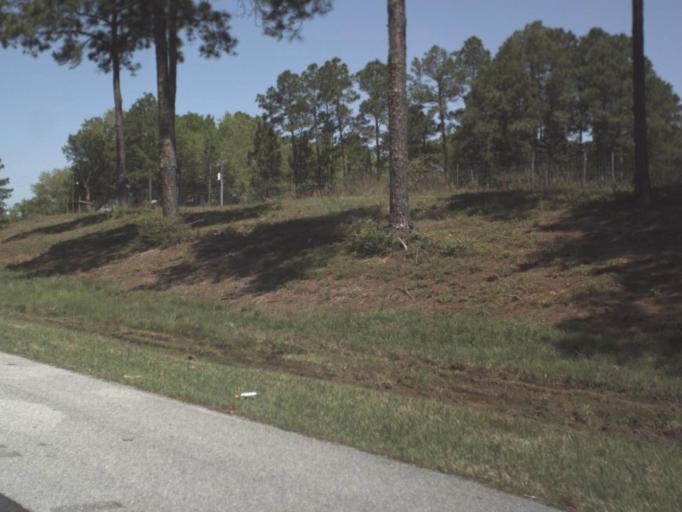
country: US
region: Florida
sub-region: Escambia County
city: Ensley
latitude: 30.5187
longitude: -87.3081
